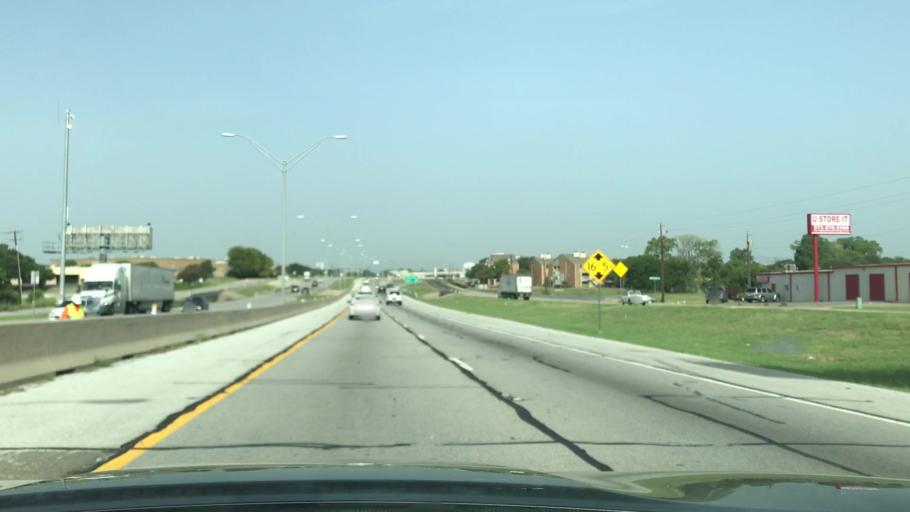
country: US
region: Texas
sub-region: Dallas County
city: Mesquite
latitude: 32.7925
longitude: -96.6467
